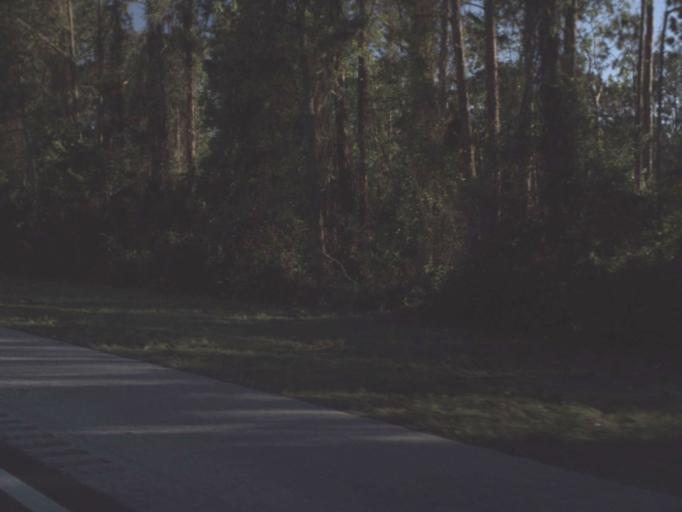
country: US
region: Florida
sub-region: Flagler County
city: Flagler Beach
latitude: 29.4170
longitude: -81.1611
